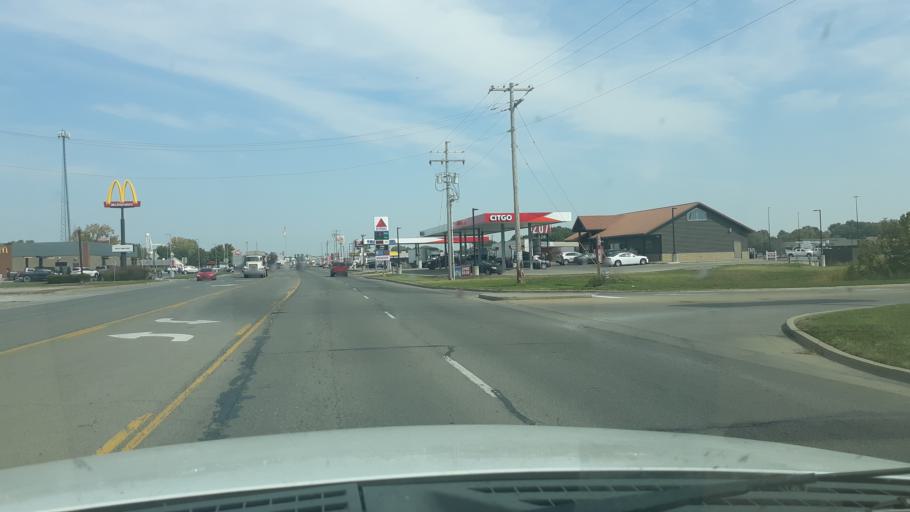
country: US
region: Illinois
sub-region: Saline County
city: Harrisburg
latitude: 37.7279
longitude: -88.5367
